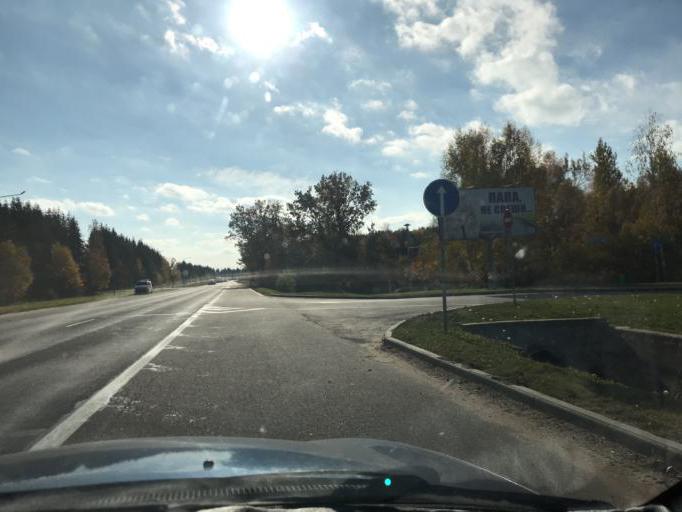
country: LT
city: Salcininkai
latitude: 54.2364
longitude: 25.3557
